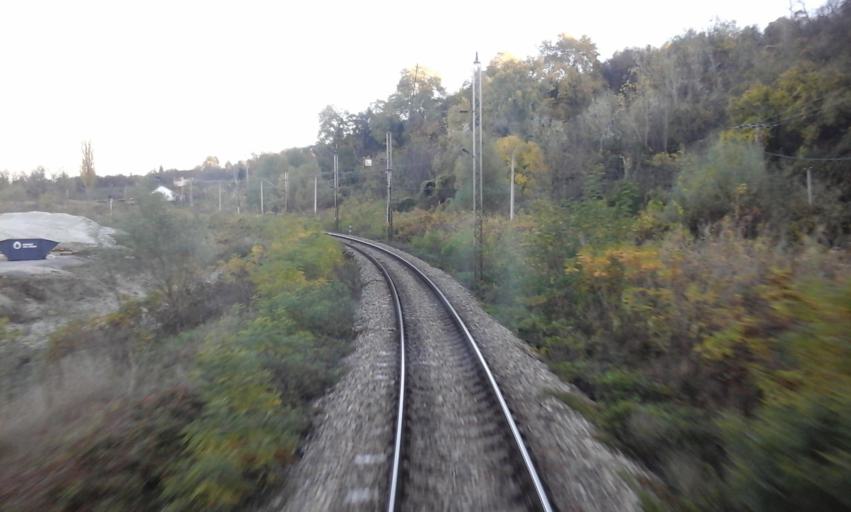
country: RS
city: Cortanovci
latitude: 45.1766
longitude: 19.9757
